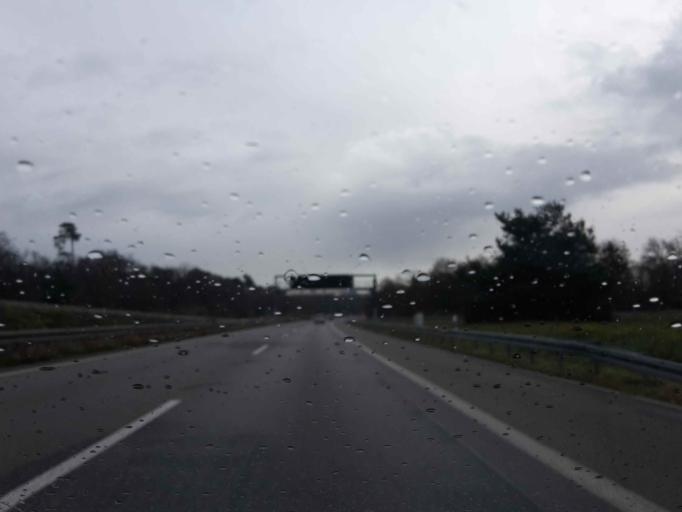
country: DE
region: Hesse
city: Griesheim
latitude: 49.8690
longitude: 8.5859
